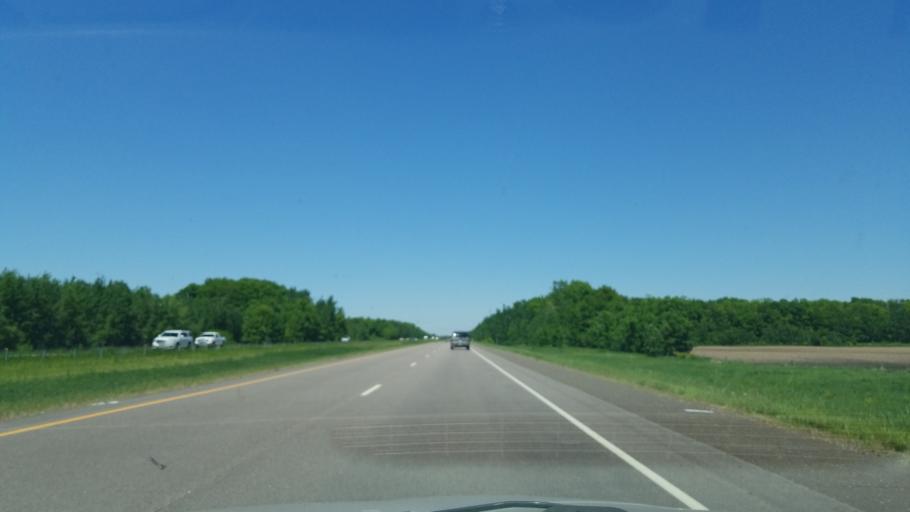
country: US
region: Minnesota
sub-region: Chisago County
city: Rush City
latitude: 45.6558
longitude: -92.9921
